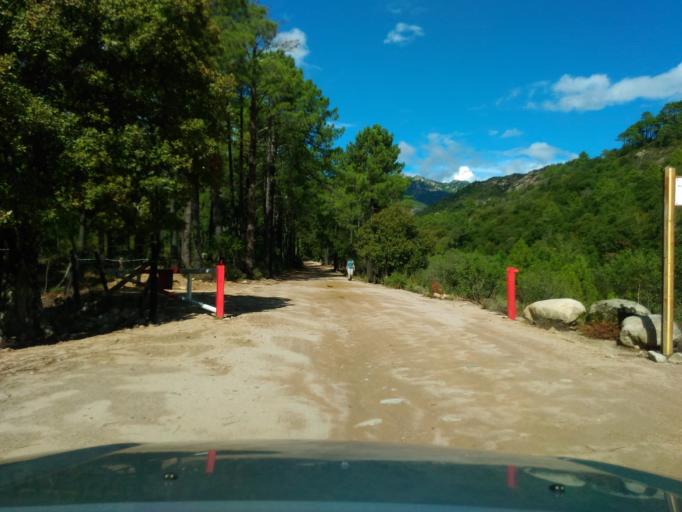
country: FR
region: Corsica
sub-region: Departement de la Corse-du-Sud
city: Zonza
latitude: 41.7216
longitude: 9.3002
